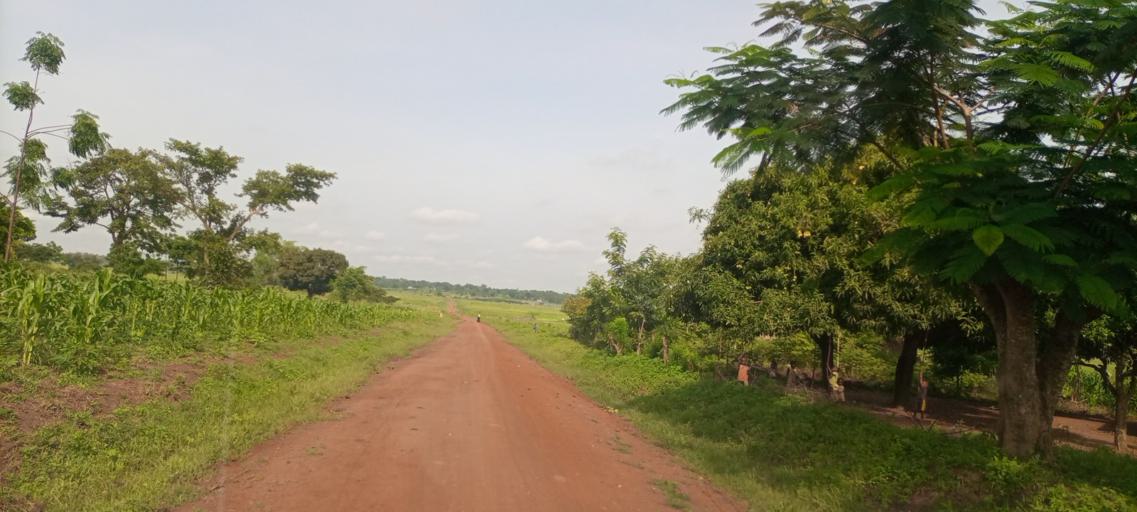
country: UG
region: Eastern Region
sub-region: Kibuku District
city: Kibuku
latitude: 1.1027
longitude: 33.7794
